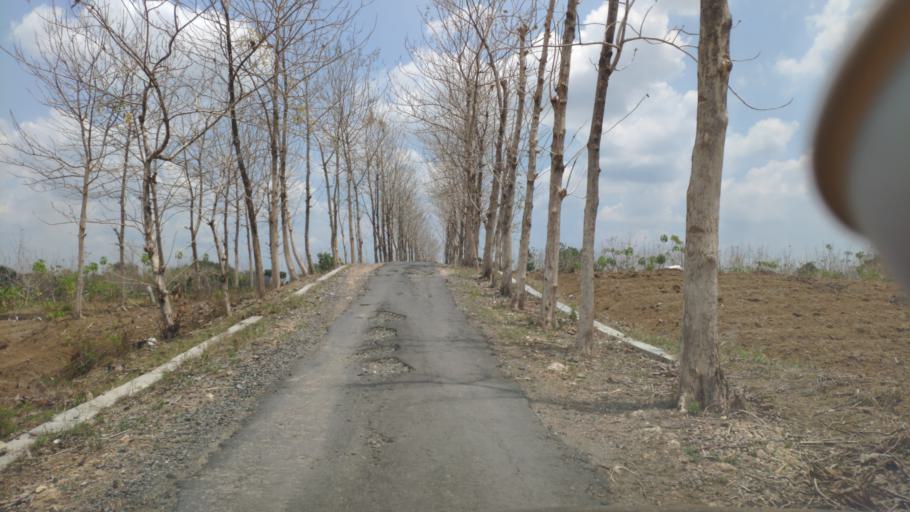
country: ID
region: Central Java
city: Bacem
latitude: -7.0501
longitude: 111.3651
